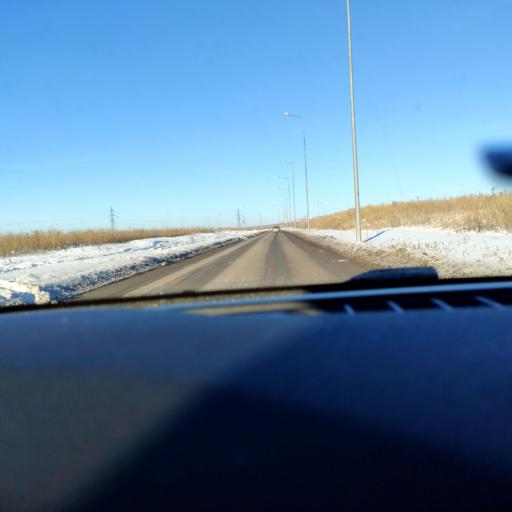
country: RU
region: Samara
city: Petra-Dubrava
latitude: 53.3090
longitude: 50.3445
